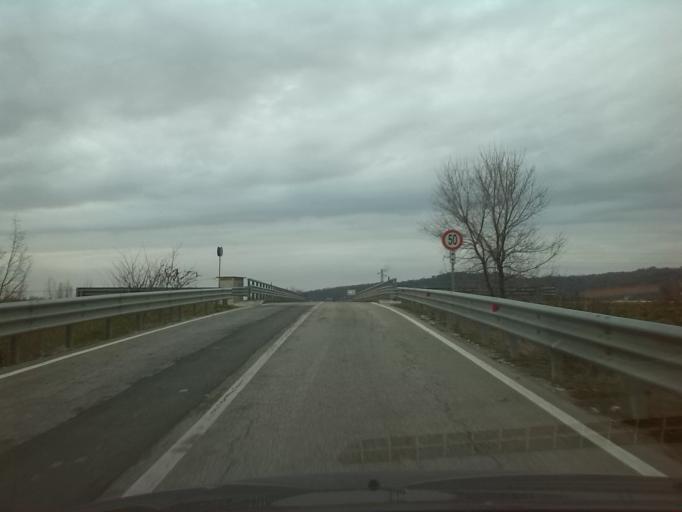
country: IT
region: Friuli Venezia Giulia
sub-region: Provincia di Gorizia
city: Medea
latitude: 45.9090
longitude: 13.4374
